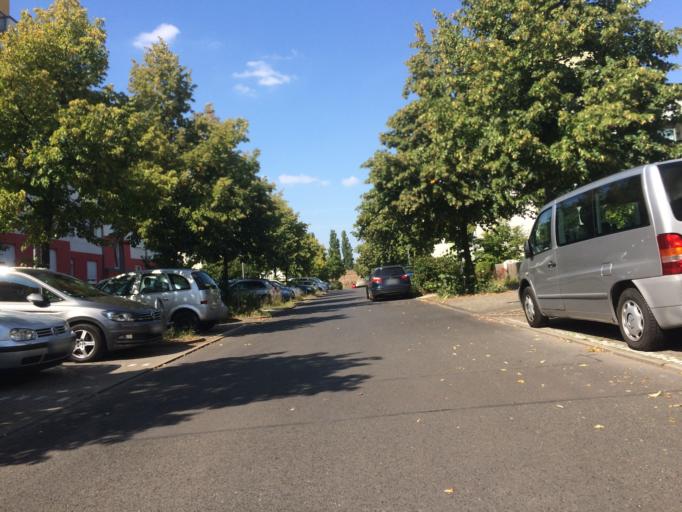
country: DE
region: Berlin
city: Niederschonhausen
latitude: 52.5889
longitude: 13.4041
